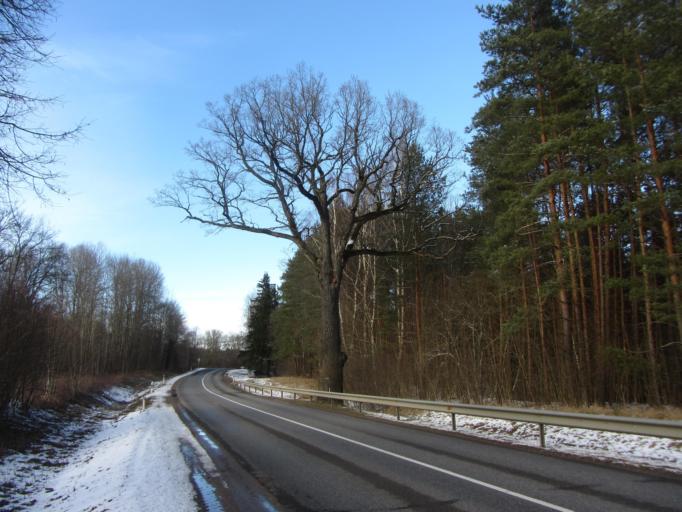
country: LT
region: Vilnius County
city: Ukmerge
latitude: 55.3518
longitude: 24.8909
